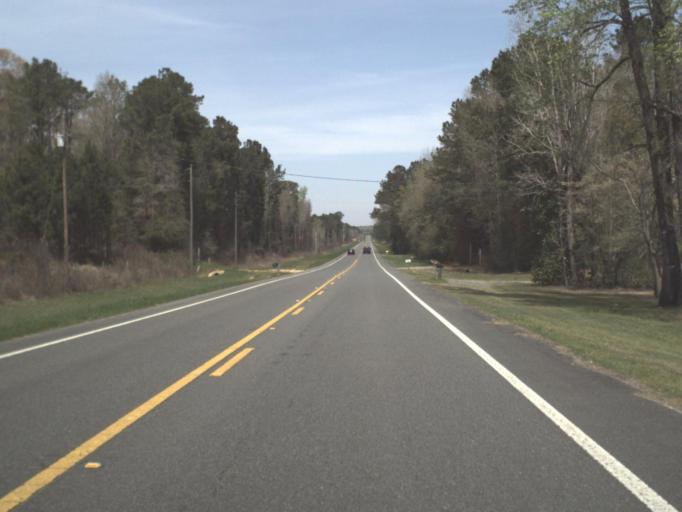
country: US
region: Florida
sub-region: Walton County
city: DeFuniak Springs
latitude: 30.7922
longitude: -85.9585
